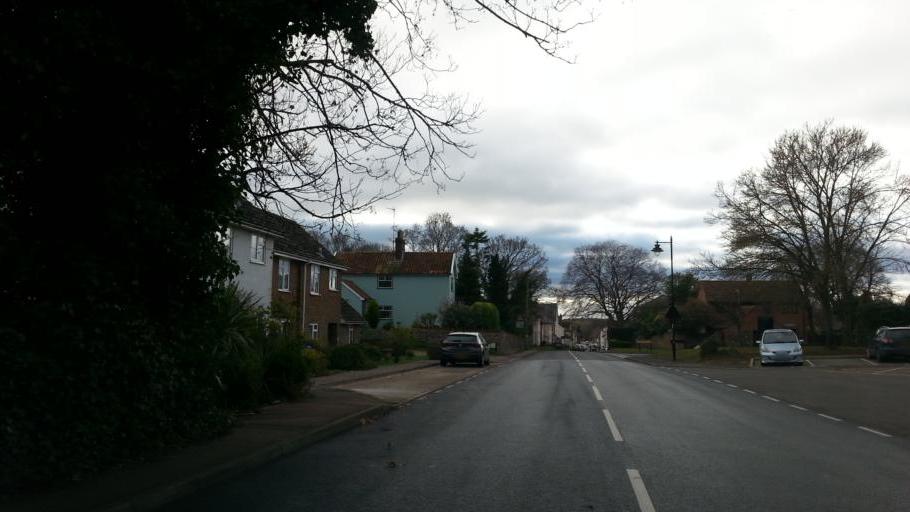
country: GB
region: England
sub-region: Suffolk
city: Ixworth
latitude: 52.3015
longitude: 0.8358
